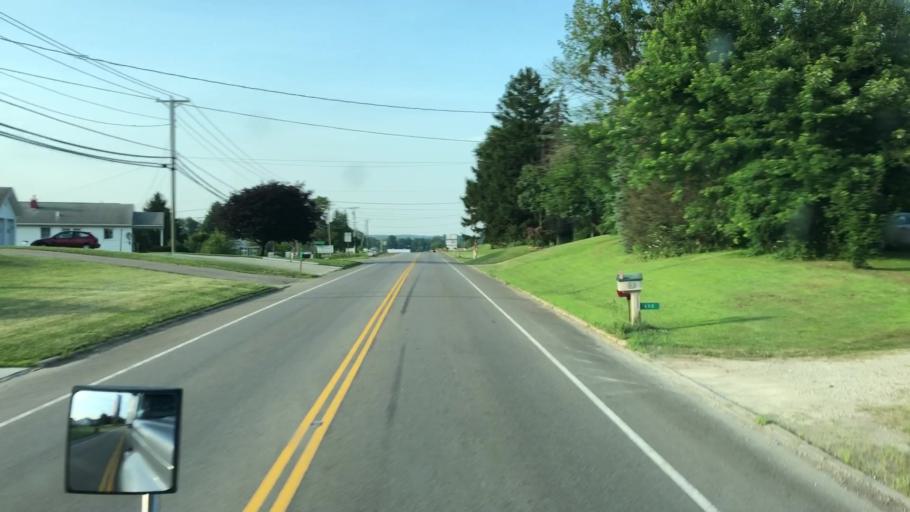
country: US
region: Ohio
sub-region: Muskingum County
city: Pleasant Grove
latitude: 39.9617
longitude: -81.9586
